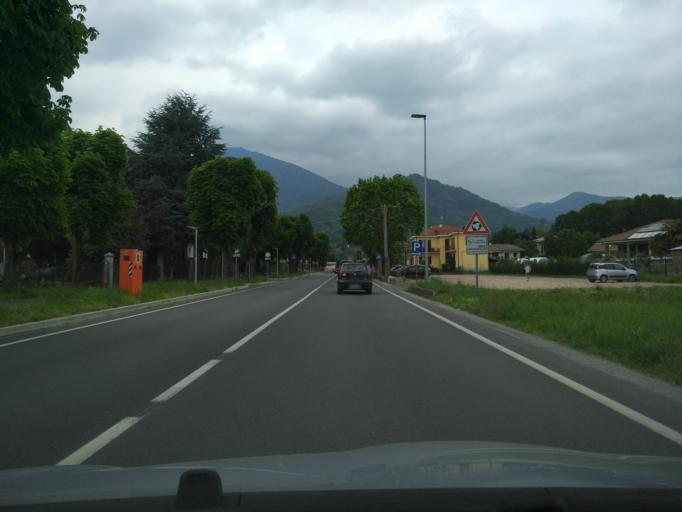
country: IT
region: Piedmont
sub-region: Provincia di Torino
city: Luserna
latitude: 44.8169
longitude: 7.2388
